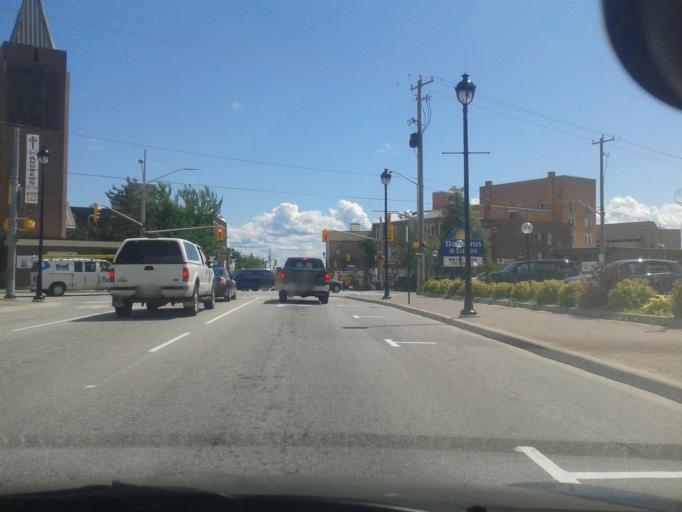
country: CA
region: Ontario
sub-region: Nipissing District
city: North Bay
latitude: 46.3140
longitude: -79.4662
